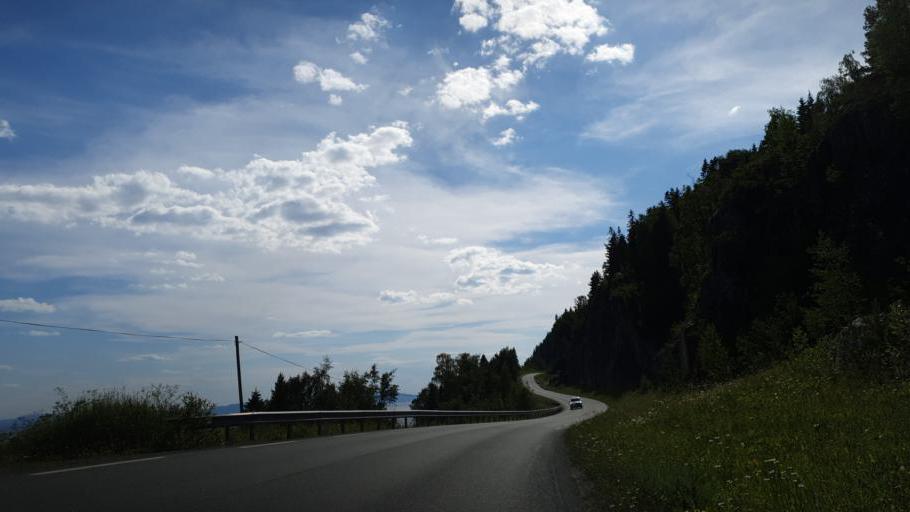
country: NO
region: Nord-Trondelag
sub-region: Leksvik
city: Leksvik
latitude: 63.6209
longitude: 10.5277
